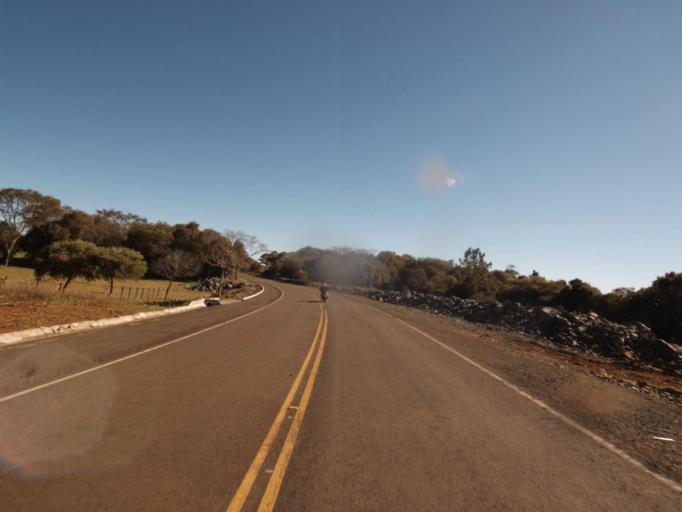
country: AR
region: Misiones
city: Bernardo de Irigoyen
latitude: -26.6129
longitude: -53.7003
